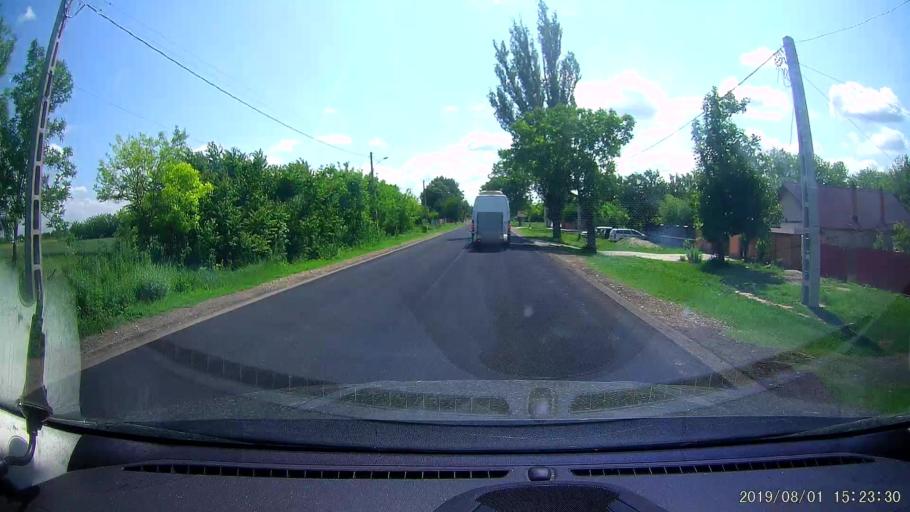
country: RO
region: Braila
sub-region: Comuna Viziru
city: Lanurile
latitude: 45.0406
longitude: 27.7594
